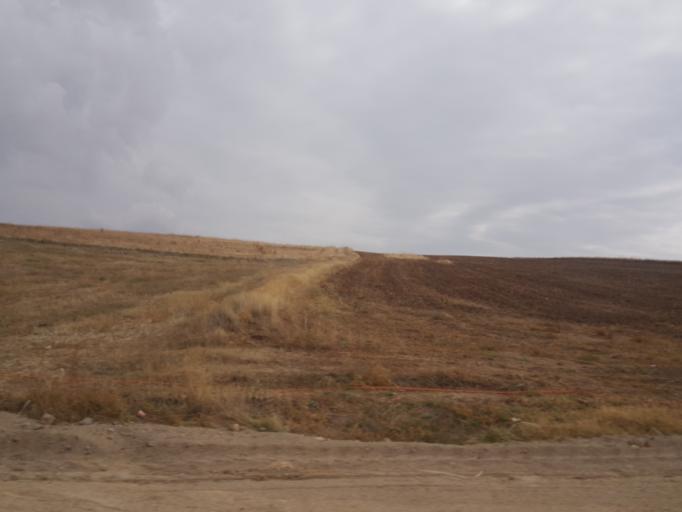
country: TR
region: Kirikkale
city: Celebi
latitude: 39.4941
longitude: 33.5431
